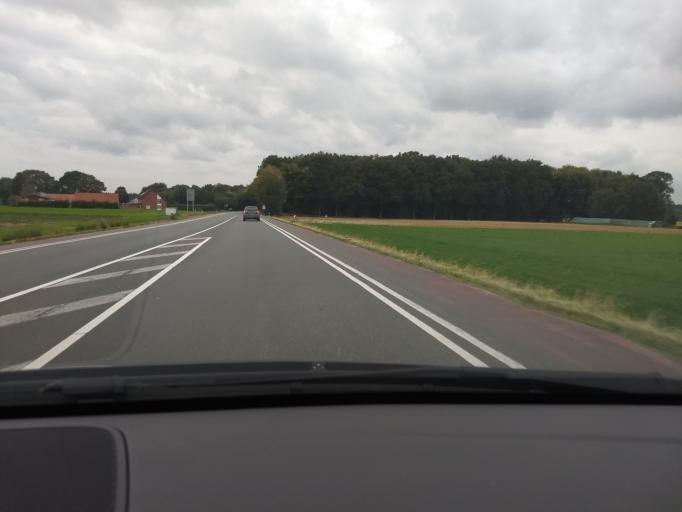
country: DE
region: North Rhine-Westphalia
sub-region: Regierungsbezirk Munster
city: Heiden
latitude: 51.8246
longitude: 6.9122
